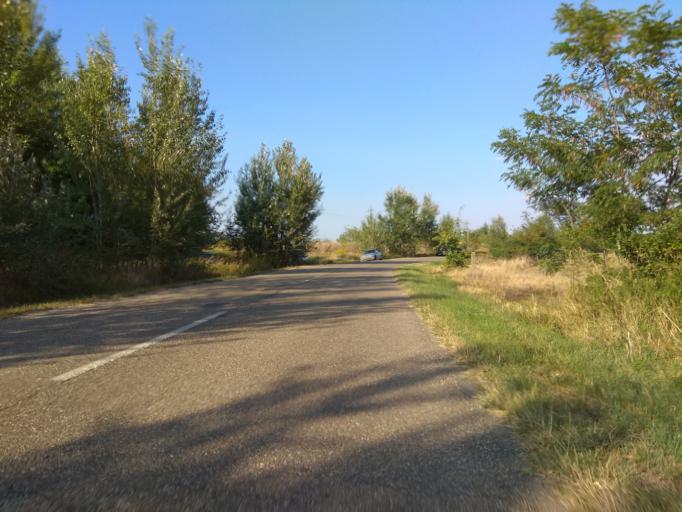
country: HU
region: Borsod-Abauj-Zemplen
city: Onod
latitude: 47.9699
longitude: 20.8862
